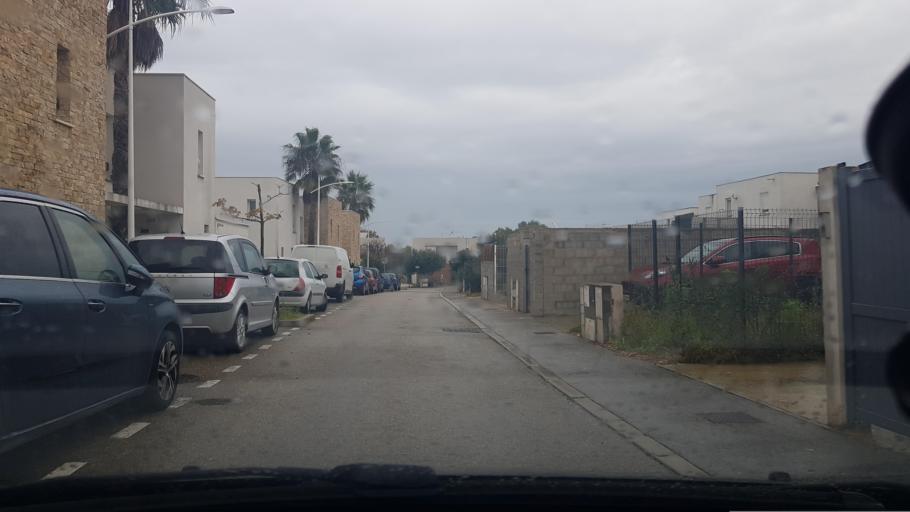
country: FR
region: Languedoc-Roussillon
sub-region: Departement du Gard
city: Bellegarde
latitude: 43.7531
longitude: 4.4988
